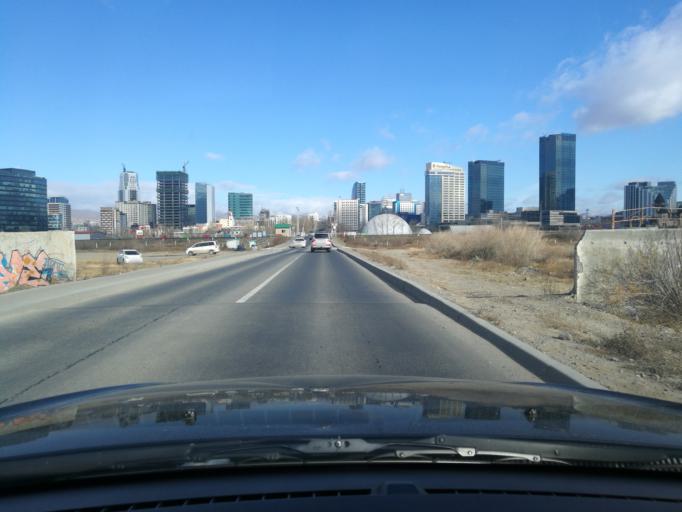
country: MN
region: Ulaanbaatar
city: Ulaanbaatar
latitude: 47.9062
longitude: 106.9183
